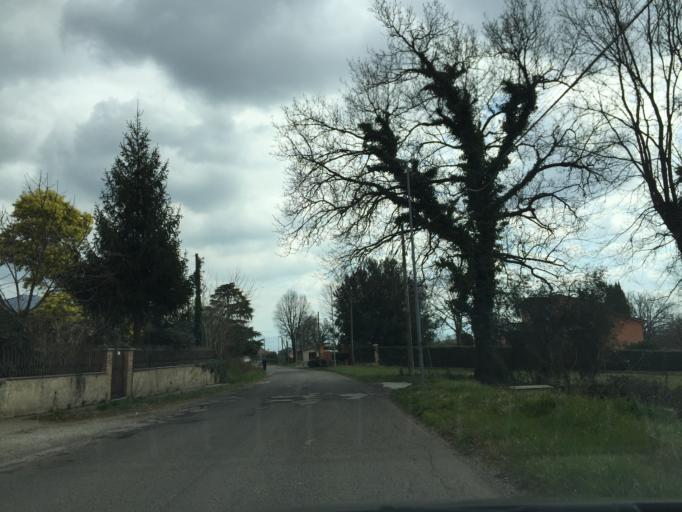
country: IT
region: Latium
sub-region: Provincia di Frosinone
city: Piedimonte San Germano Alta
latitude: 41.5007
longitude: 13.7396
